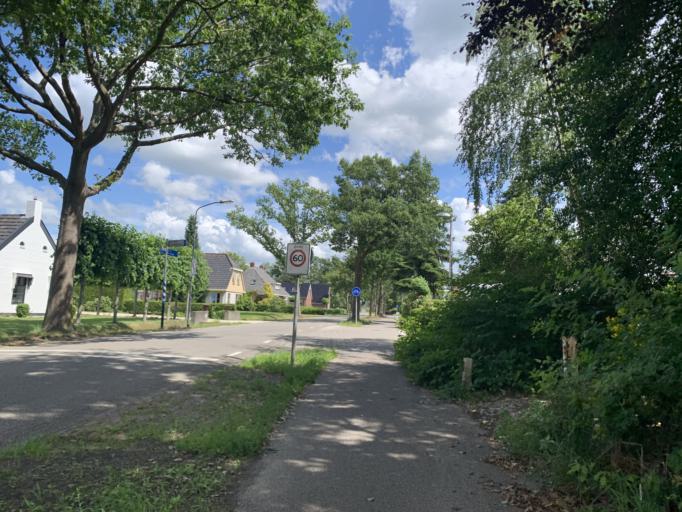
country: NL
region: Groningen
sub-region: Gemeente Haren
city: Haren
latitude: 53.1640
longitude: 6.6288
